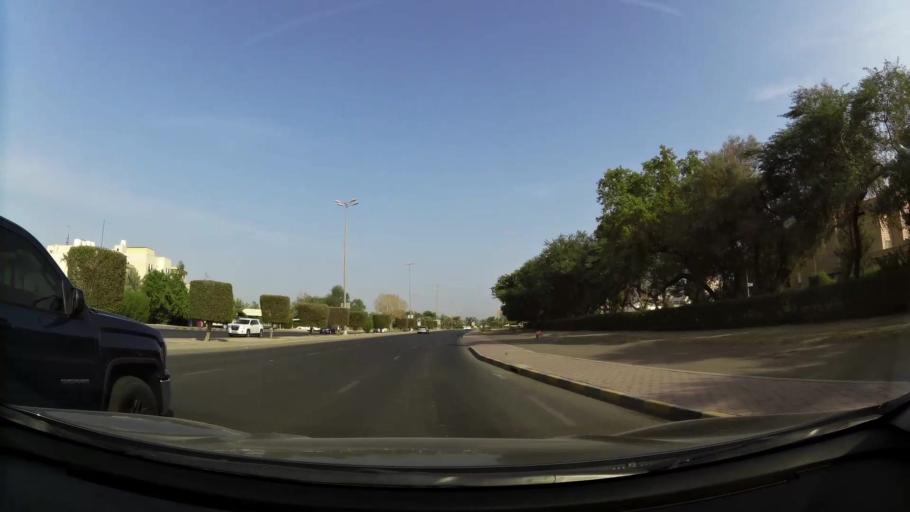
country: KW
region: Mubarak al Kabir
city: Mubarak al Kabir
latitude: 29.1749
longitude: 48.0818
